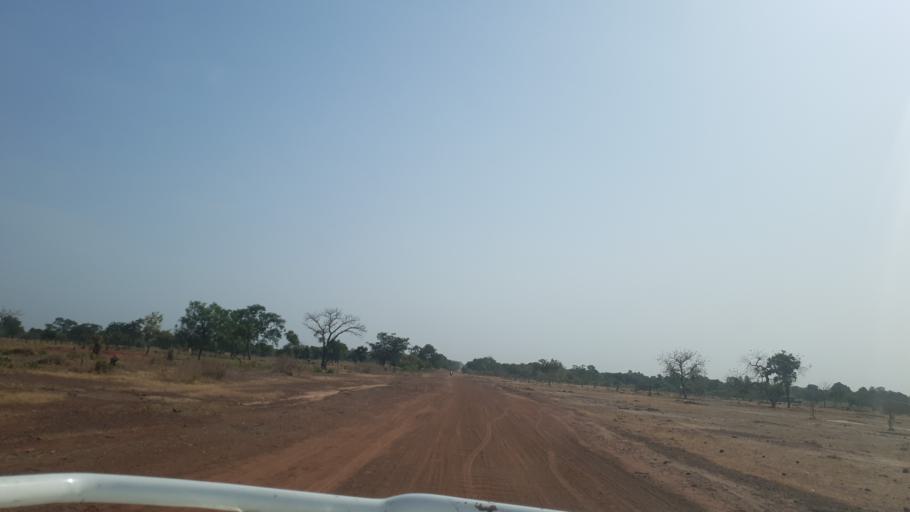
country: ML
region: Koulikoro
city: Dioila
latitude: 12.6680
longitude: -6.6895
